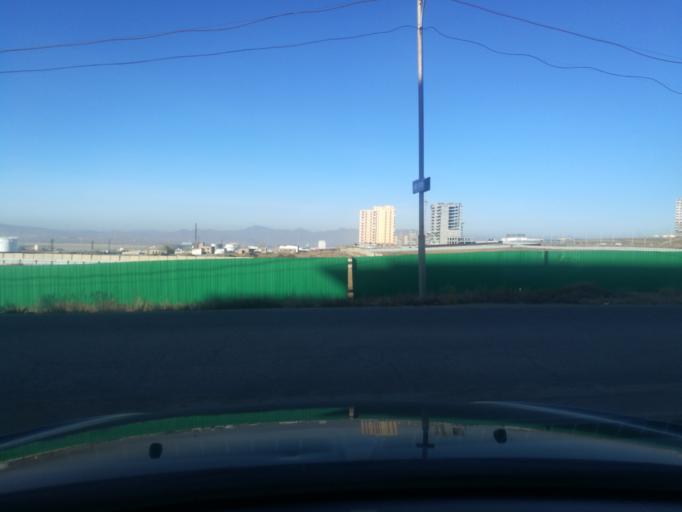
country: MN
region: Ulaanbaatar
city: Ulaanbaatar
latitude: 47.8542
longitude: 106.7802
